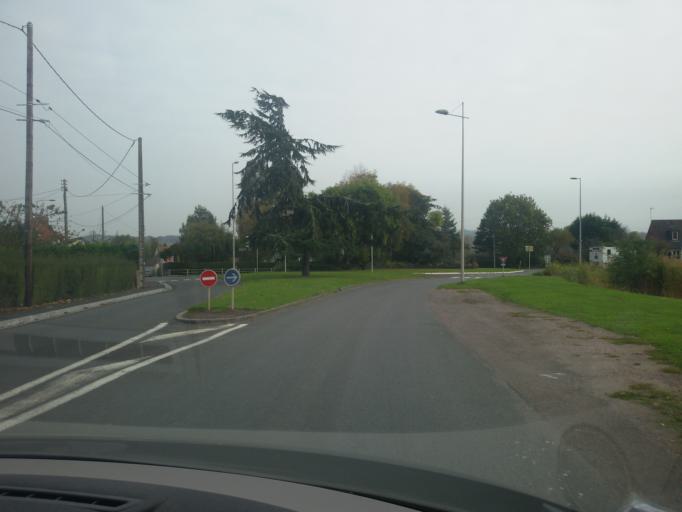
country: FR
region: Lower Normandy
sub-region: Departement du Calvados
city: Cabourg
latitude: 49.2827
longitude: -0.1177
